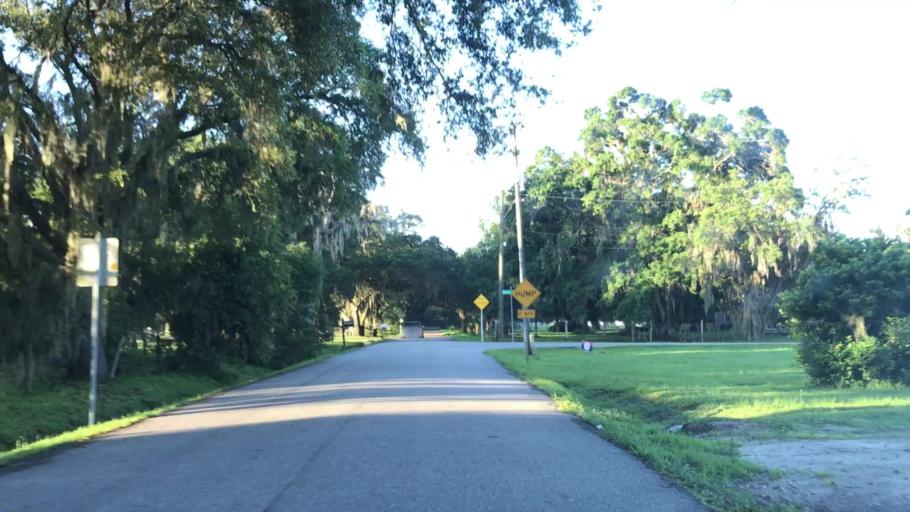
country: US
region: Florida
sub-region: Sarasota County
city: Lake Sarasota
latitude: 27.3313
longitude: -82.4083
